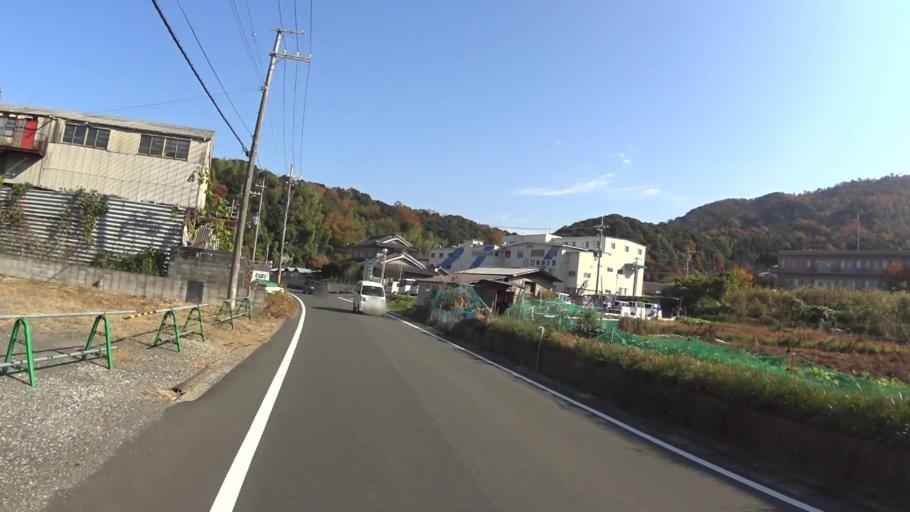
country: JP
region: Kyoto
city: Maizuru
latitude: 35.4731
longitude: 135.3407
